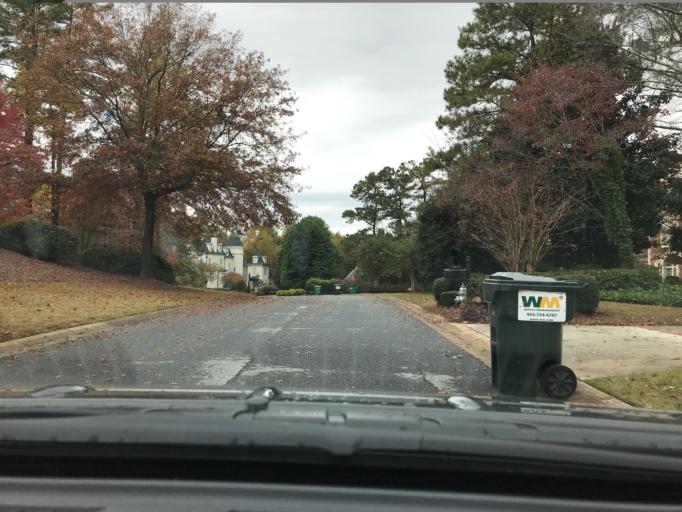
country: US
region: Georgia
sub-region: Fulton County
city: Johns Creek
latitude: 34.0134
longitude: -84.2495
